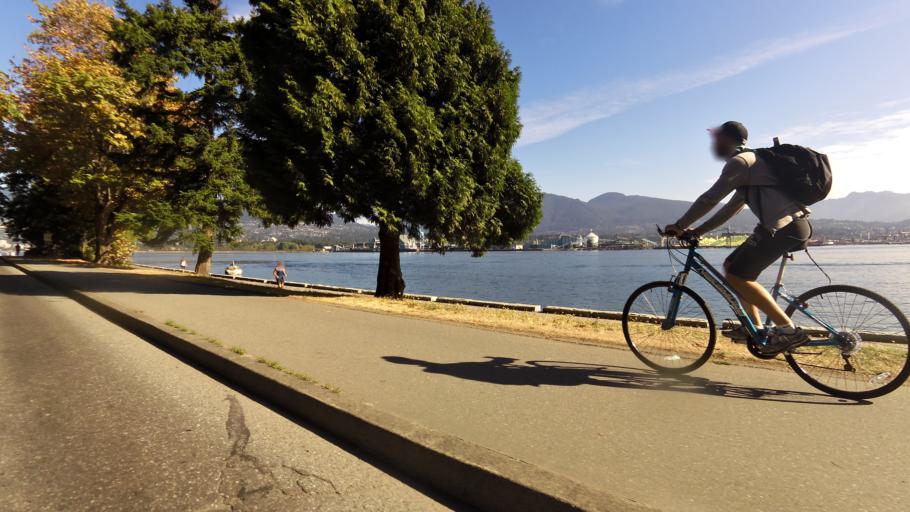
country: CA
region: British Columbia
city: West End
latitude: 49.3017
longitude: -123.1255
